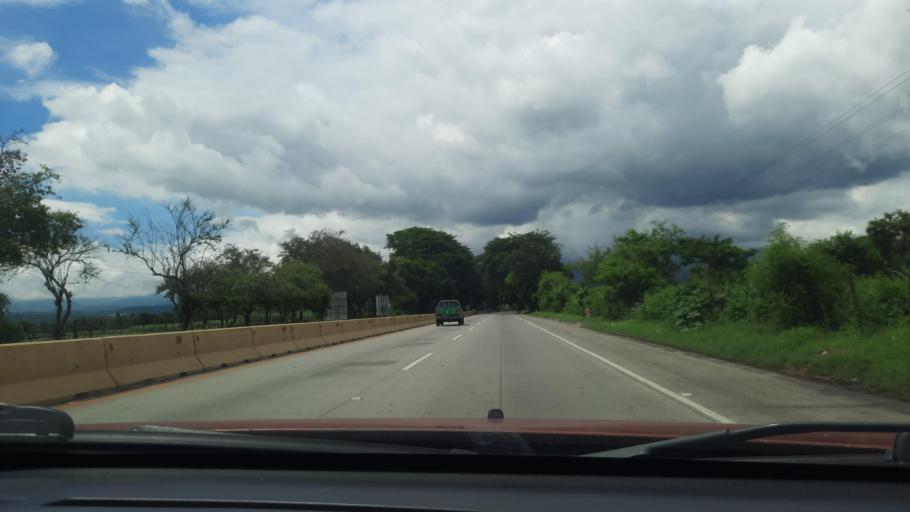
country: SV
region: Sonsonate
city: Sonsonate
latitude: 13.7139
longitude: -89.7100
